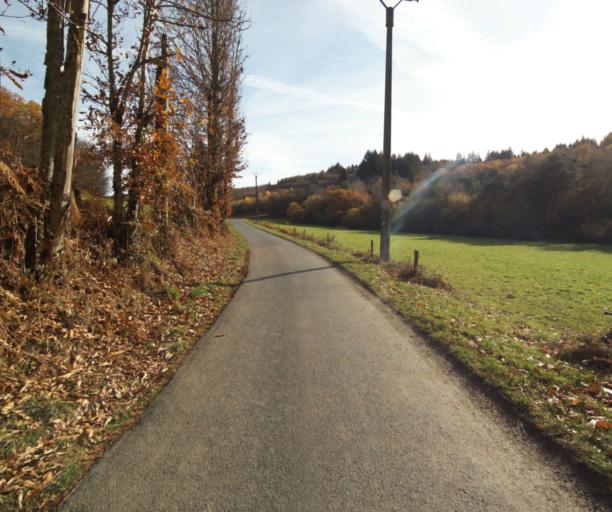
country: FR
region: Limousin
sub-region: Departement de la Correze
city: Sainte-Fortunade
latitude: 45.1990
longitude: 1.7510
